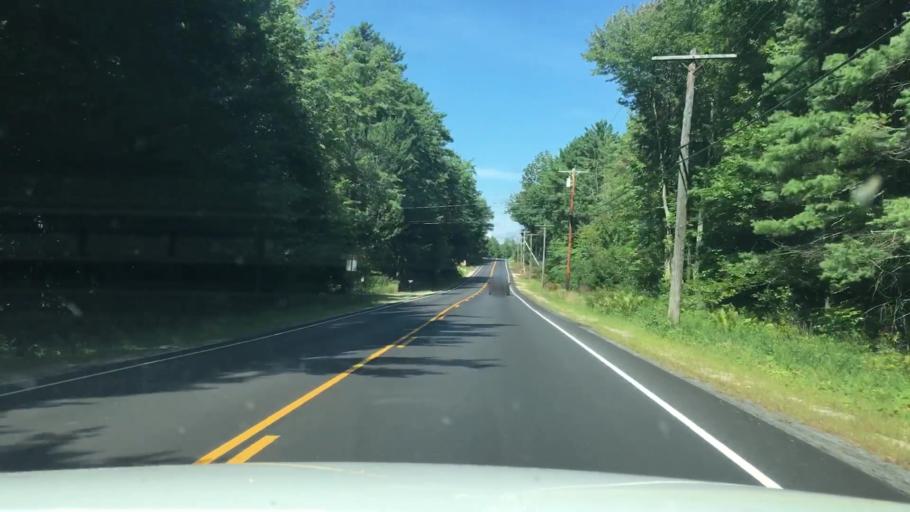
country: US
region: Maine
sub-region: Cumberland County
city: Cumberland Center
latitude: 43.8379
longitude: -70.3212
